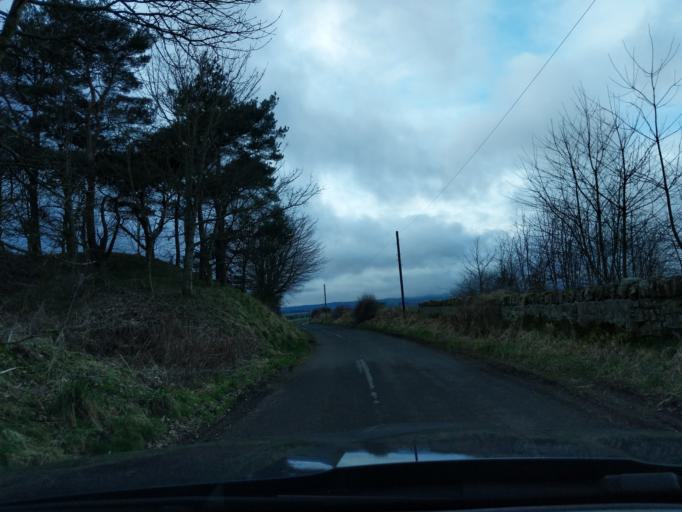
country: GB
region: England
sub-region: Northumberland
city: Ford
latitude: 55.7117
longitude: -2.1010
